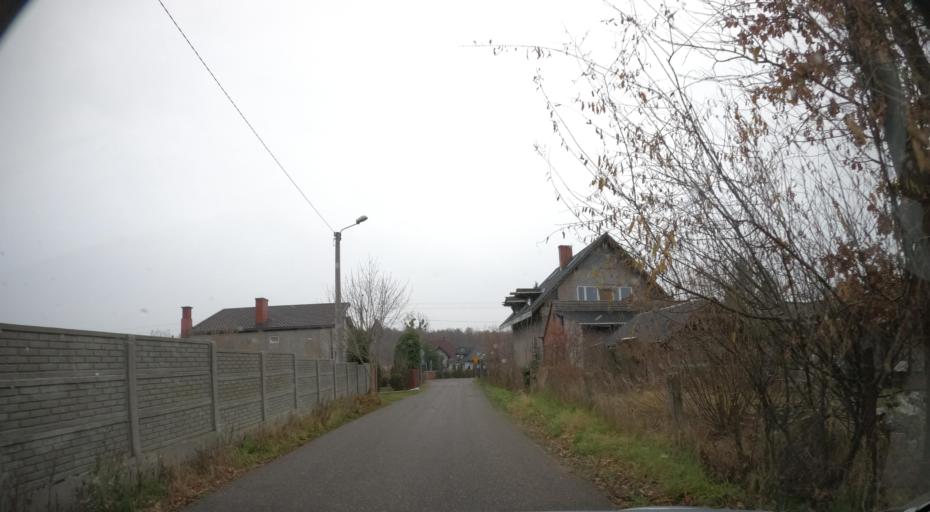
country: PL
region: Masovian Voivodeship
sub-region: Powiat radomski
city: Jastrzebia
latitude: 51.4287
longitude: 21.2319
